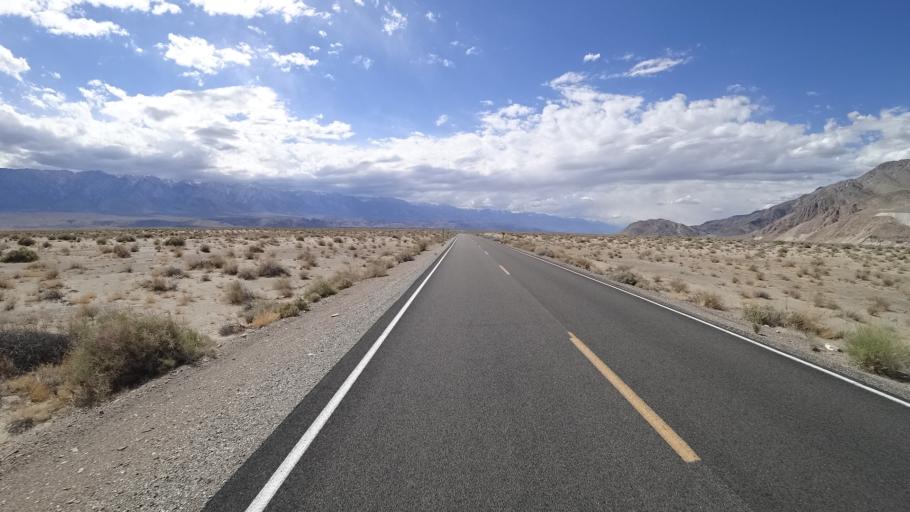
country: US
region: California
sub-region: Inyo County
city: Lone Pine
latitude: 36.5547
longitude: -117.9579
